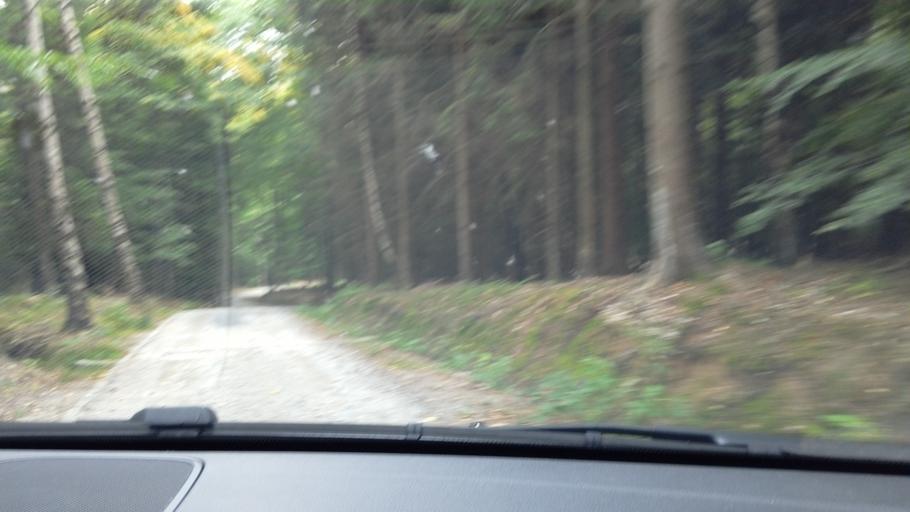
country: PL
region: Lower Silesian Voivodeship
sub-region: Powiat jeleniogorski
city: Karpacz
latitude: 50.7665
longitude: 15.7512
